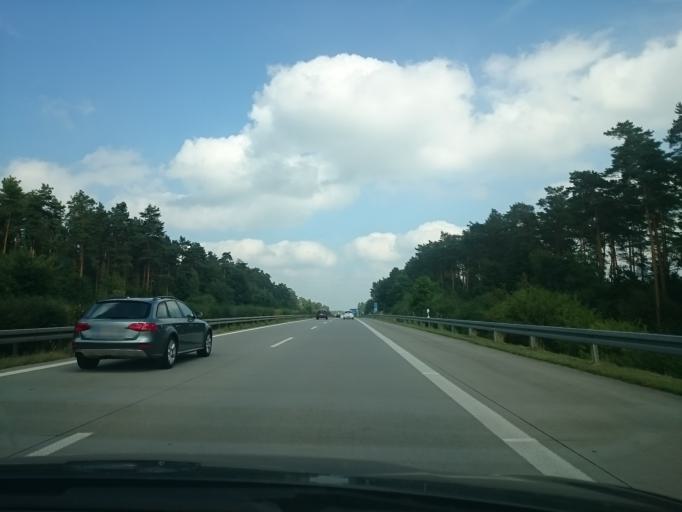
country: DE
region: Brandenburg
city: Rudnitz
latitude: 52.7694
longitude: 13.5583
